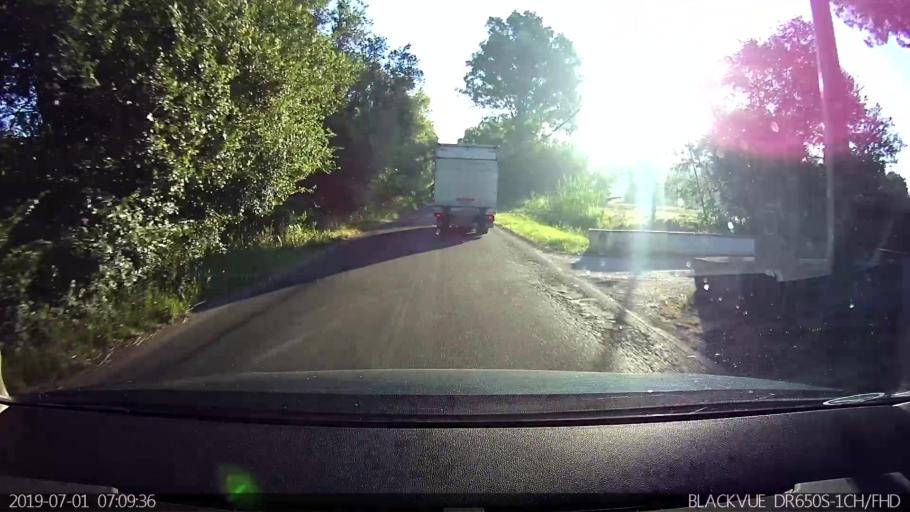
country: IT
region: Latium
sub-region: Provincia di Latina
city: Borgo Hermada
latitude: 41.3065
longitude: 13.1626
